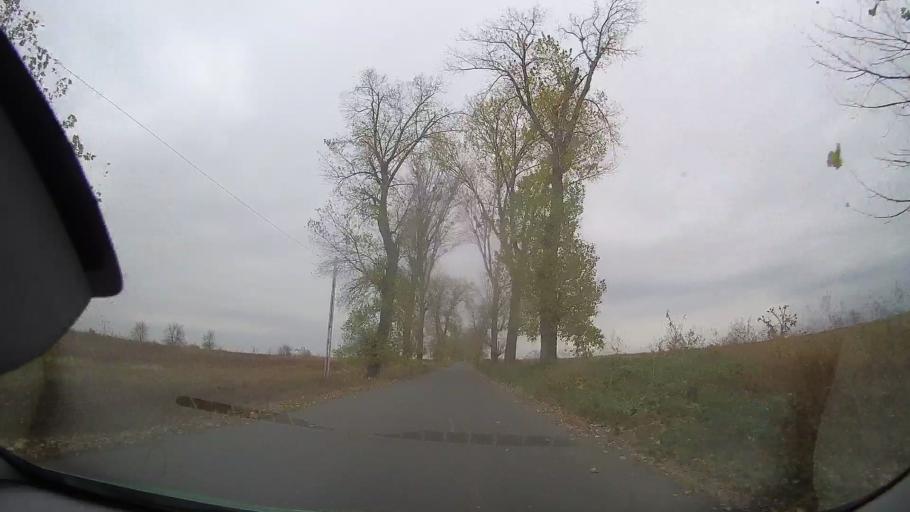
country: RO
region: Braila
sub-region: Comuna Ciocile
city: Ciocile
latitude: 44.8083
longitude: 27.2798
